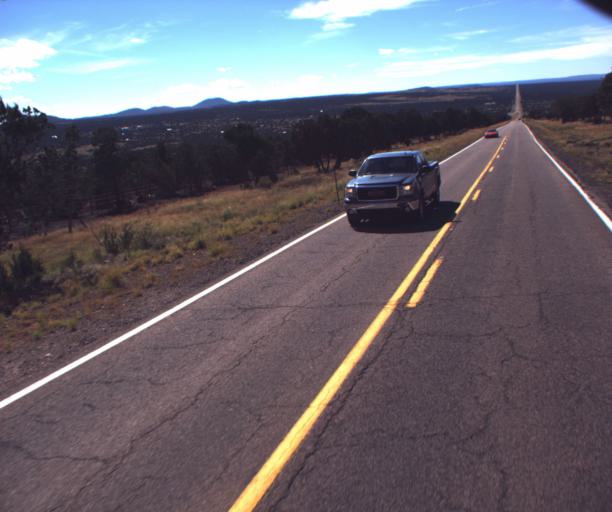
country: US
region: Arizona
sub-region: Navajo County
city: White Mountain Lake
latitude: 34.2893
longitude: -109.8178
